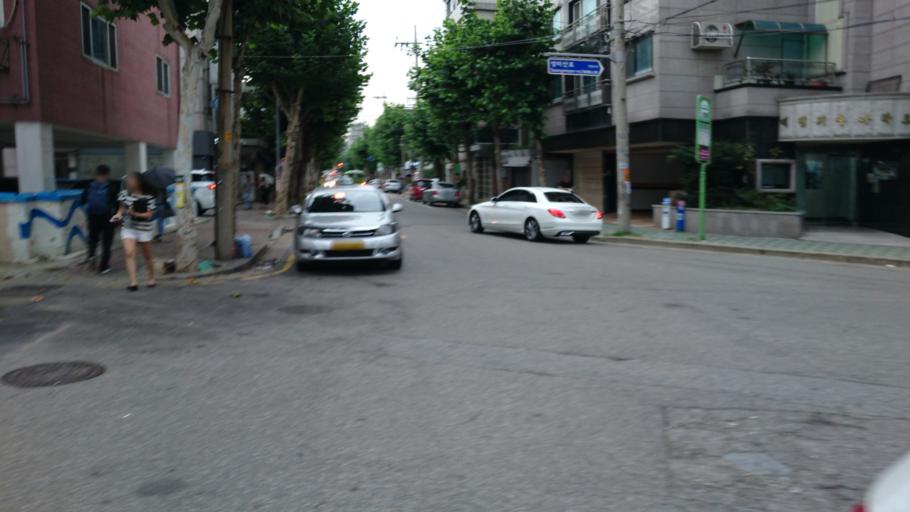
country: KR
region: Seoul
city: Seoul
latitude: 37.5648
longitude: 126.9242
